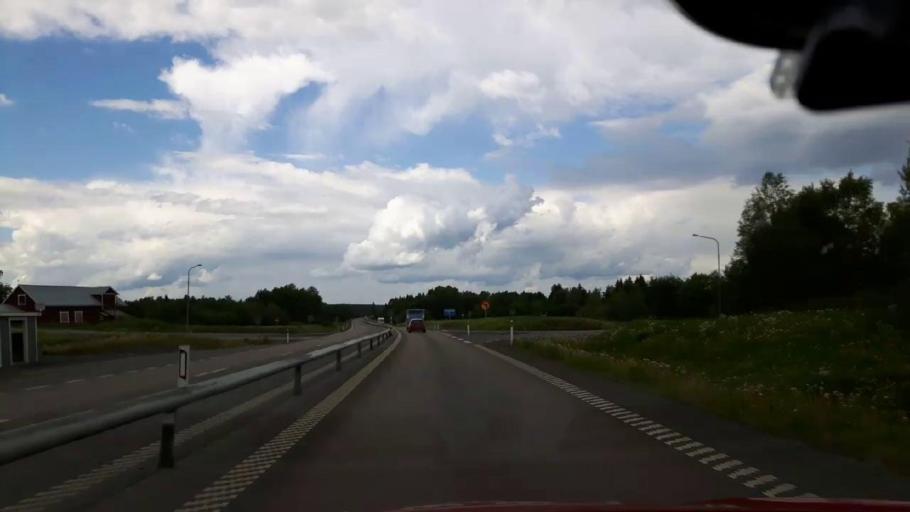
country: SE
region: Jaemtland
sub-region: Krokoms Kommun
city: Krokom
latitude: 63.3105
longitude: 14.4790
